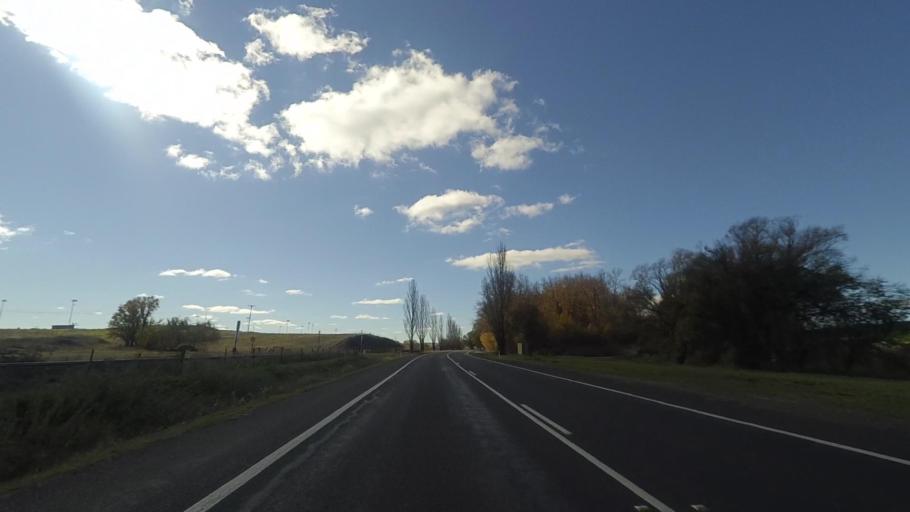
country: AU
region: New South Wales
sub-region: Bathurst Regional
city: Bathurst
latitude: -33.4551
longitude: 149.5759
